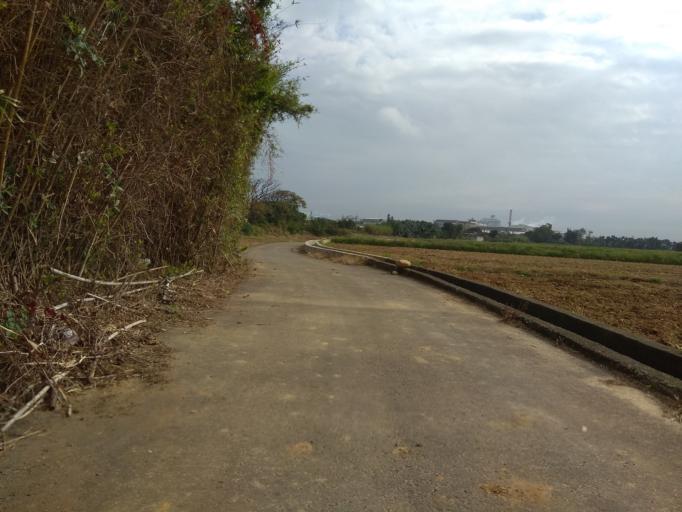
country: TW
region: Taiwan
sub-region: Hsinchu
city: Zhubei
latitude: 24.9818
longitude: 121.0329
